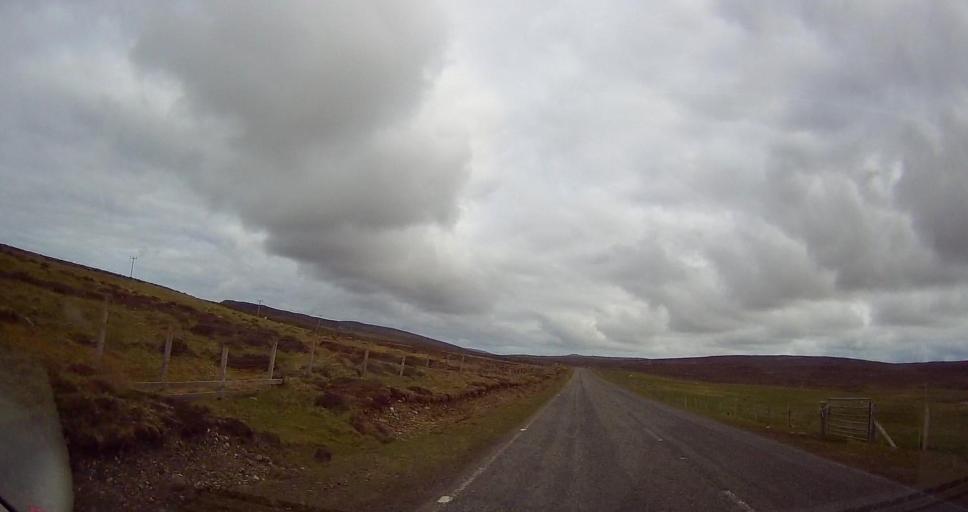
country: GB
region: Scotland
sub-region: Shetland Islands
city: Shetland
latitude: 60.6973
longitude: -0.9222
